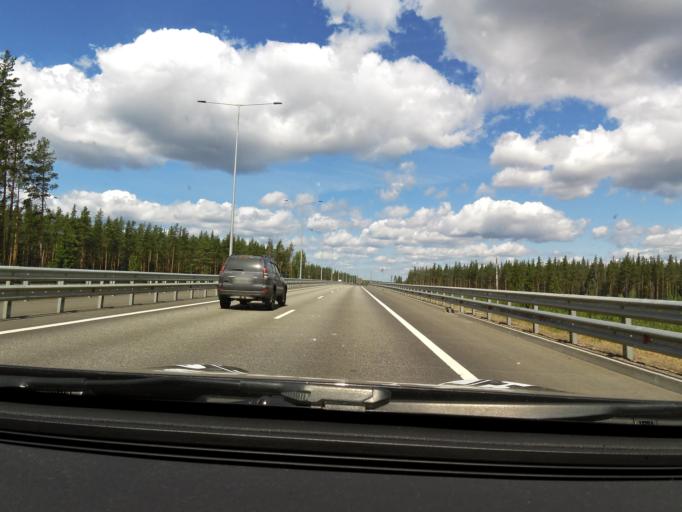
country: RU
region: Tverskaya
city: Krasnomayskiy
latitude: 57.5105
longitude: 34.2872
